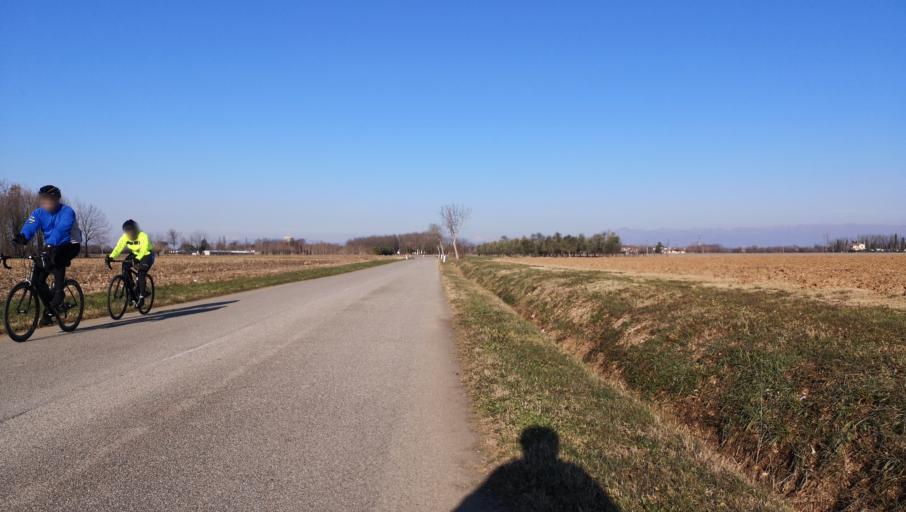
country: IT
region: Friuli Venezia Giulia
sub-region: Provincia di Udine
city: Santa Maria la Longa
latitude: 45.9470
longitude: 13.2742
